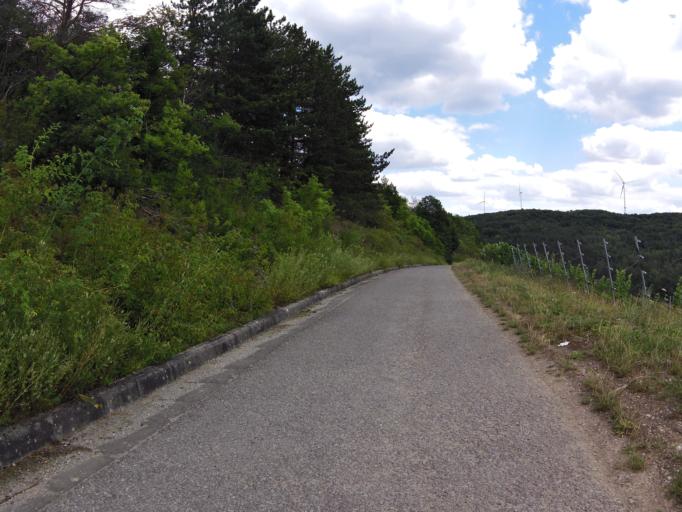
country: DE
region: Bavaria
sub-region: Regierungsbezirk Unterfranken
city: Thungersheim
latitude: 49.8846
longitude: 9.8621
